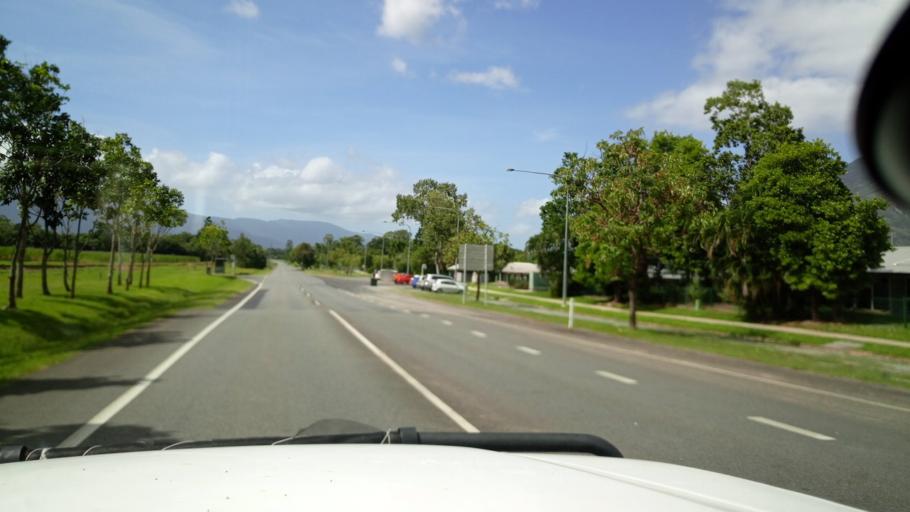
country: AU
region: Queensland
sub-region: Cairns
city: Woree
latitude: -17.0857
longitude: 145.7783
